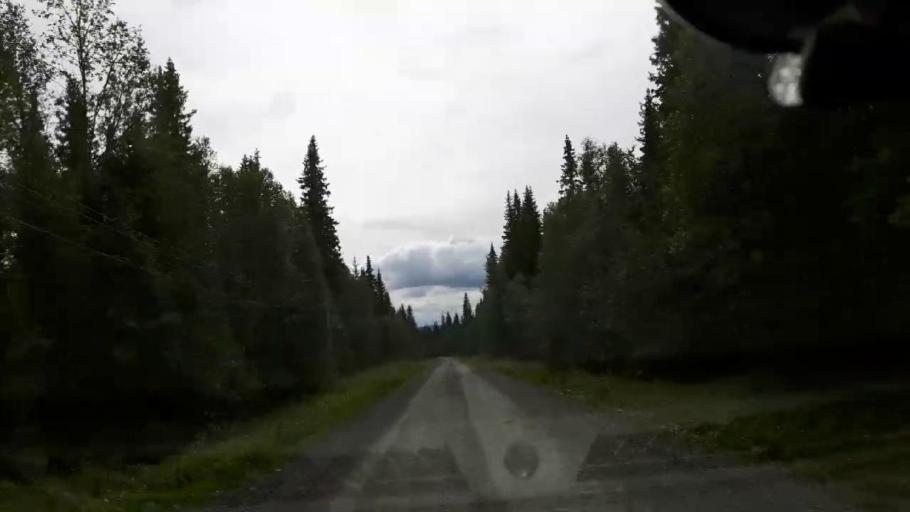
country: SE
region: Jaemtland
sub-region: Krokoms Kommun
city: Valla
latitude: 63.7155
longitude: 13.8597
